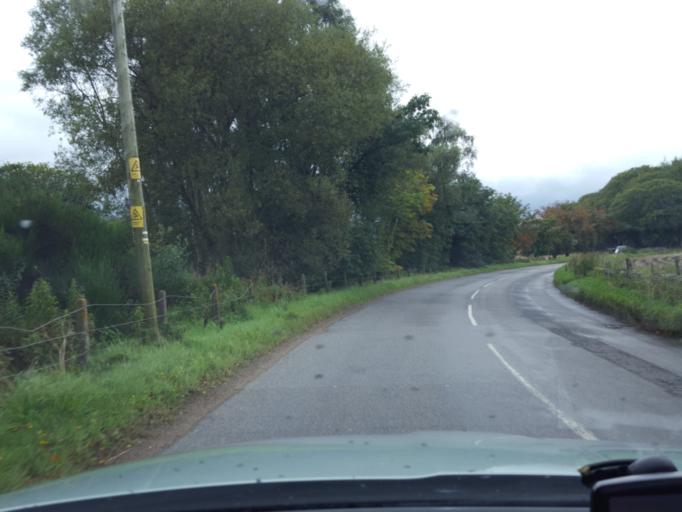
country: GB
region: Scotland
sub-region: Aberdeenshire
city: Kemnay
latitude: 57.1695
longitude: -2.4168
